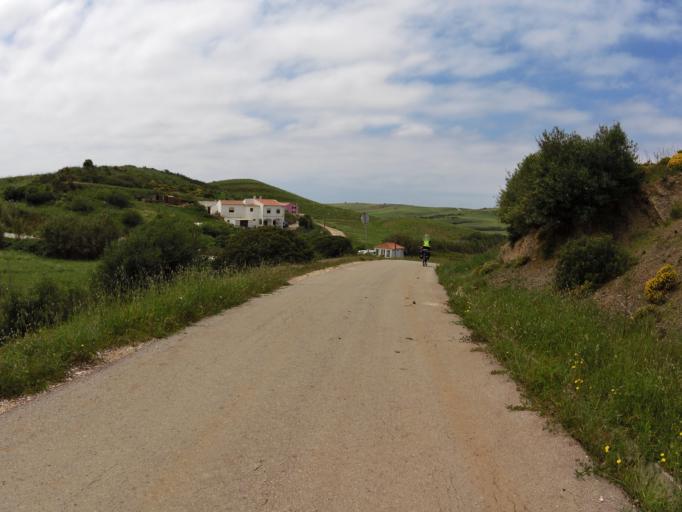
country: PT
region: Faro
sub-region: Vila do Bispo
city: Vila do Bispo
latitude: 37.0796
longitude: -8.8866
